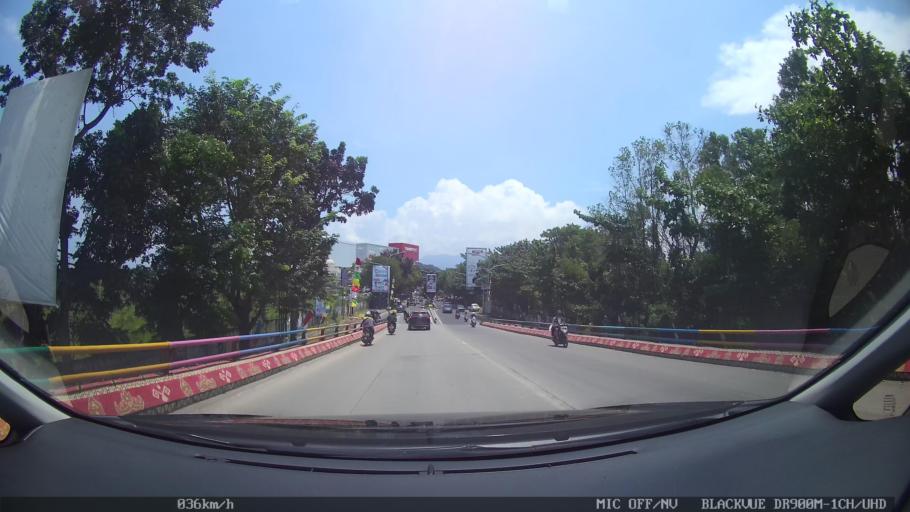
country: ID
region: Lampung
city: Kedaton
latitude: -5.3816
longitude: 105.2849
